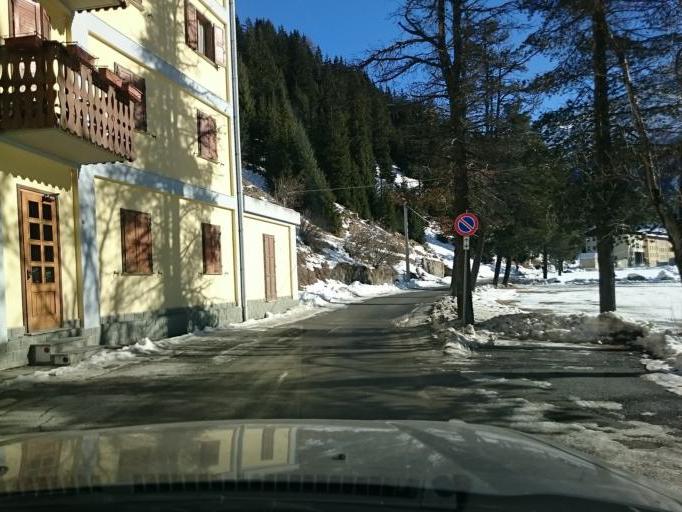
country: IT
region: Lombardy
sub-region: Provincia di Sondrio
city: Sant'Antonio
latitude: 46.4145
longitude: 10.4910
